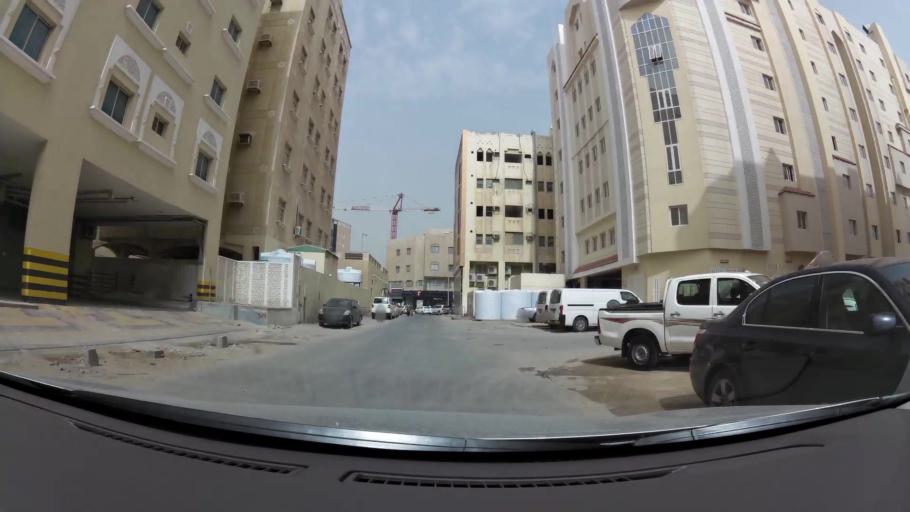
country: QA
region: Baladiyat ad Dawhah
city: Doha
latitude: 25.2702
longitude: 51.5439
